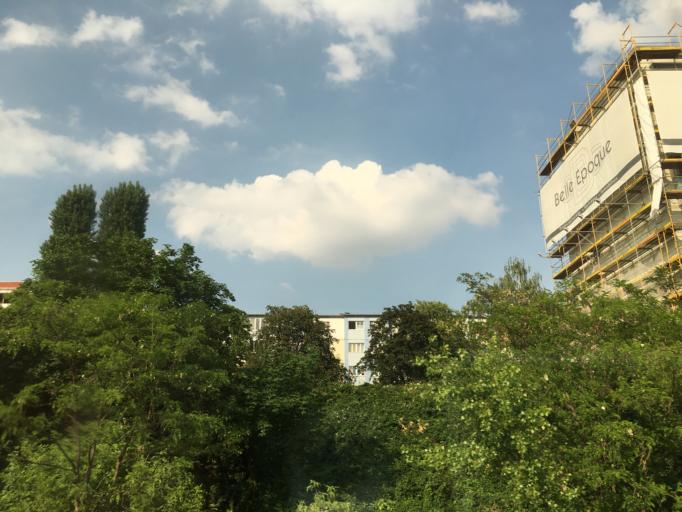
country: DE
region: Berlin
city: Halensee
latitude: 52.4949
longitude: 13.2920
